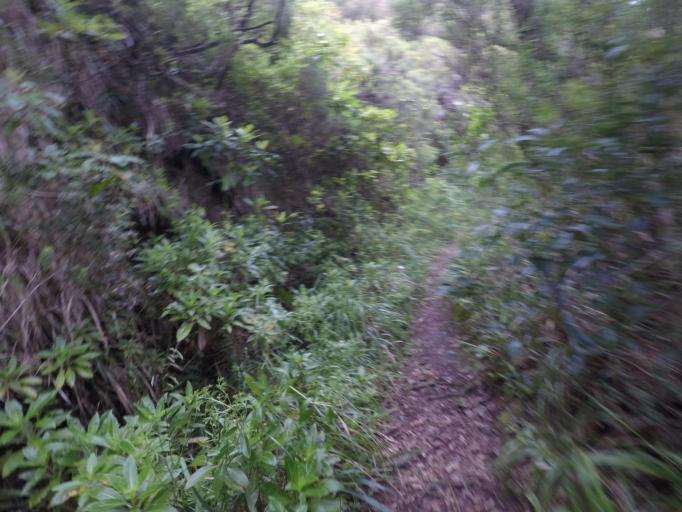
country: PT
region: Madeira
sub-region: Sao Vicente
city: Sao Vicente
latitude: 32.7685
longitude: -17.0560
